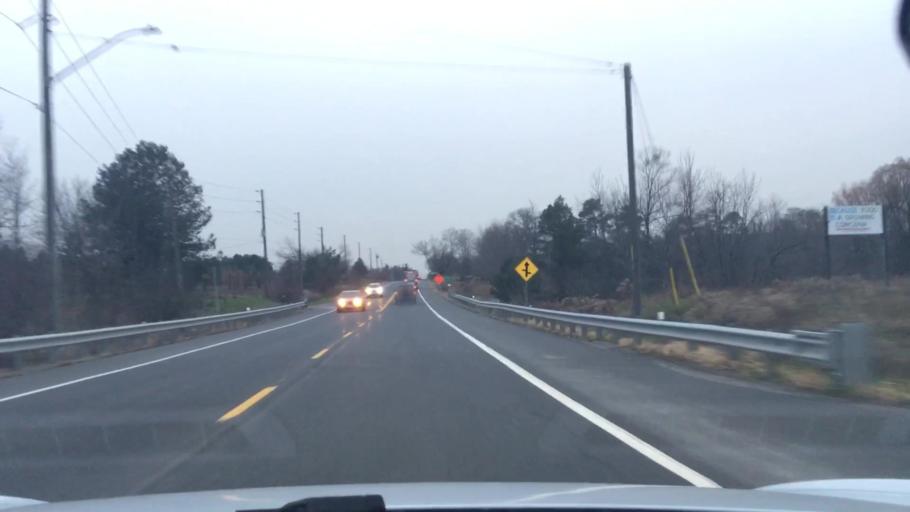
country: CA
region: Ontario
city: Pickering
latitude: 43.9173
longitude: -79.1126
